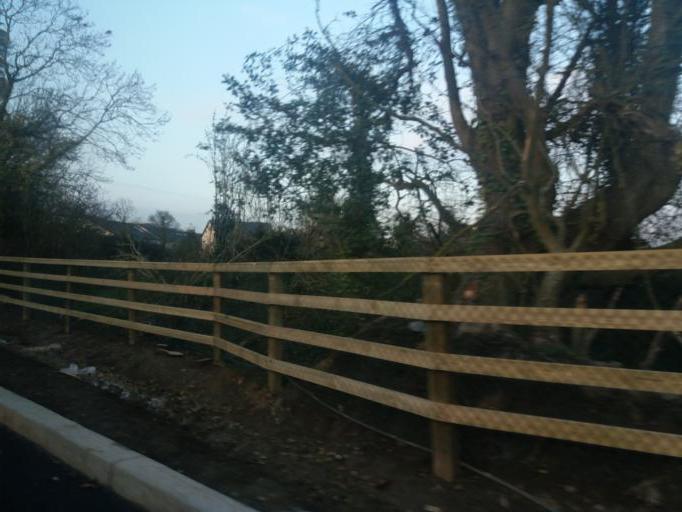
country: IE
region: Leinster
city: Hartstown
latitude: 53.3888
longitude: -6.4350
